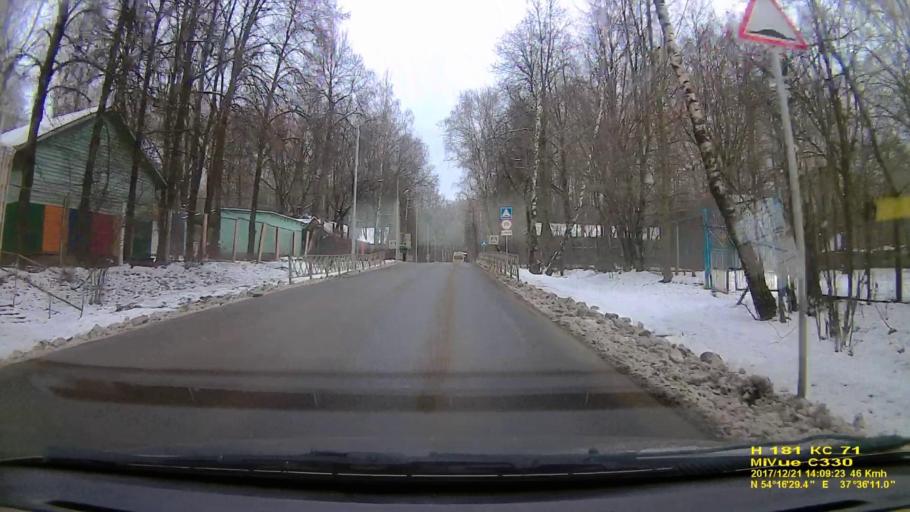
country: RU
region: Tula
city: Gorelki
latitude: 54.2749
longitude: 37.6031
